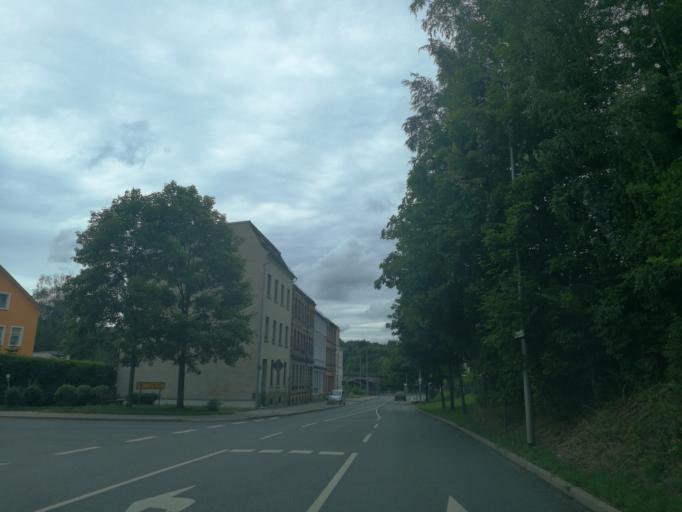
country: DE
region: Saxony
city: Adorf
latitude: 50.3199
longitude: 12.2634
